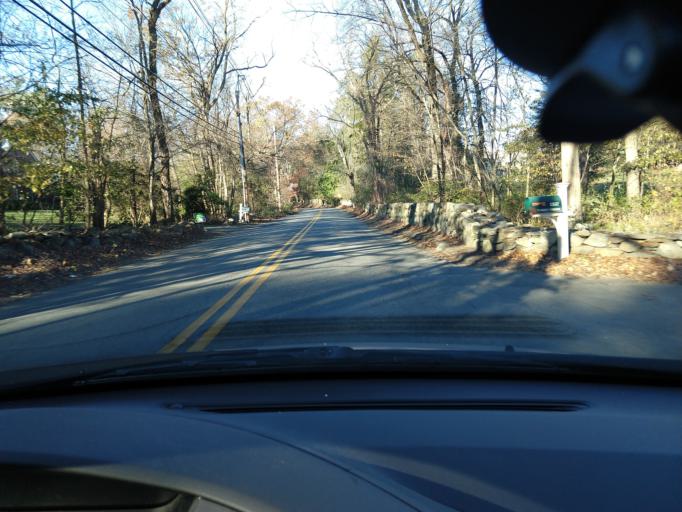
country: US
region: Massachusetts
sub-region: Middlesex County
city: Concord
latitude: 42.4910
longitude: -71.3330
